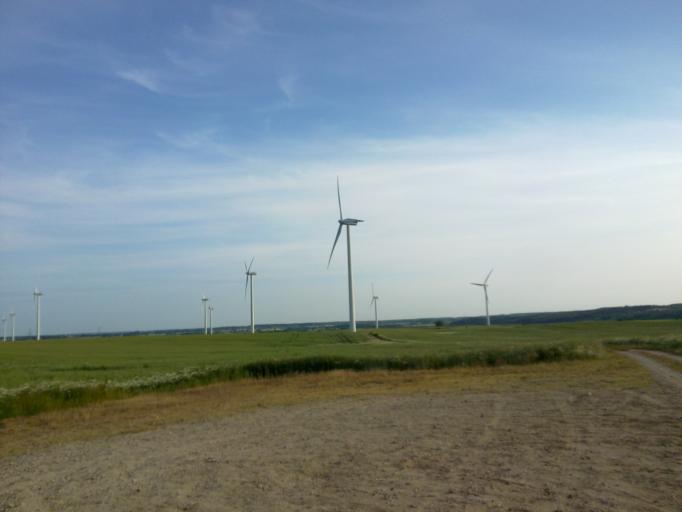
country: PL
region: Pomeranian Voivodeship
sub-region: Powiat pucki
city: Gniezdzewo
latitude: 54.7512
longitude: 18.3626
